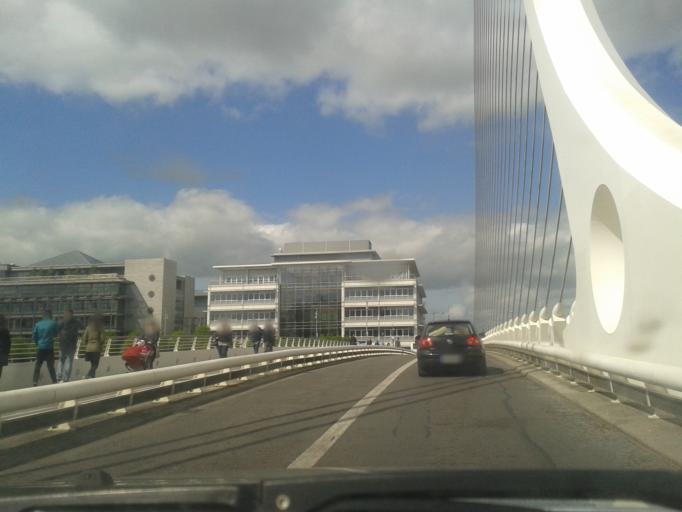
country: IE
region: Leinster
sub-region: Dublin City
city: Dublin
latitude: 53.3465
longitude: -6.2416
